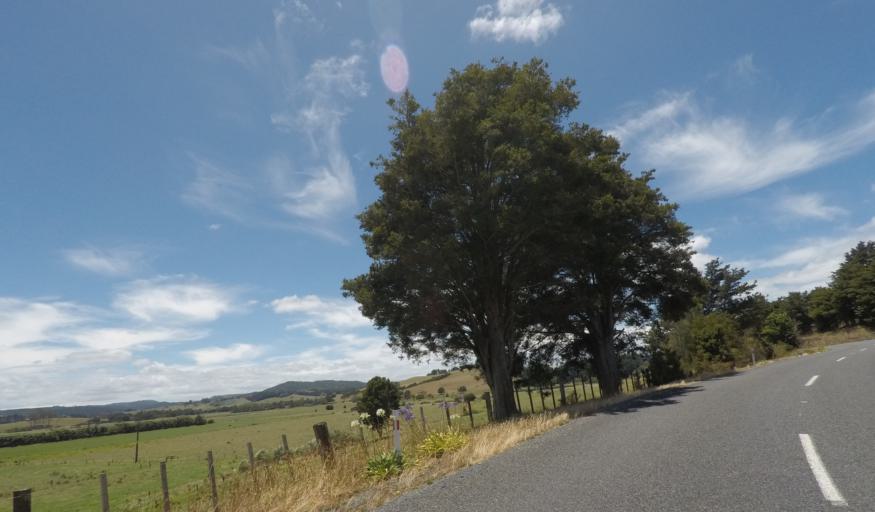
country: NZ
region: Northland
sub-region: Whangarei
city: Whangarei
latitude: -35.5495
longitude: 174.2993
